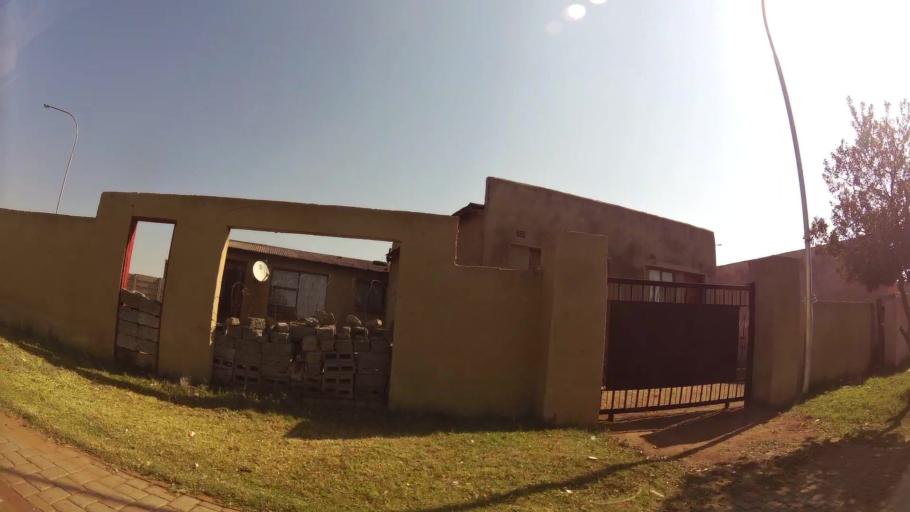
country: ZA
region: Gauteng
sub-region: Ekurhuleni Metropolitan Municipality
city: Benoni
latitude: -26.2283
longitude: 28.3082
